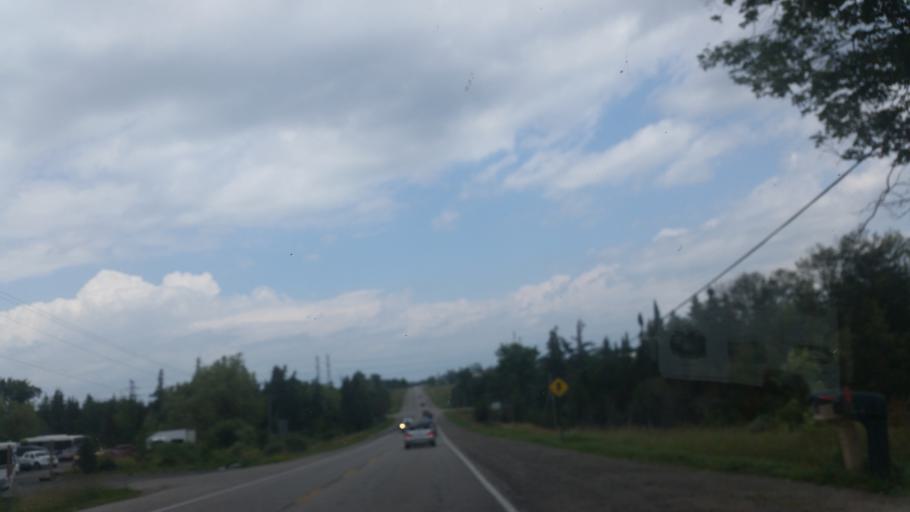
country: CA
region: Ontario
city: Orangeville
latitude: 43.7160
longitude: -80.1144
